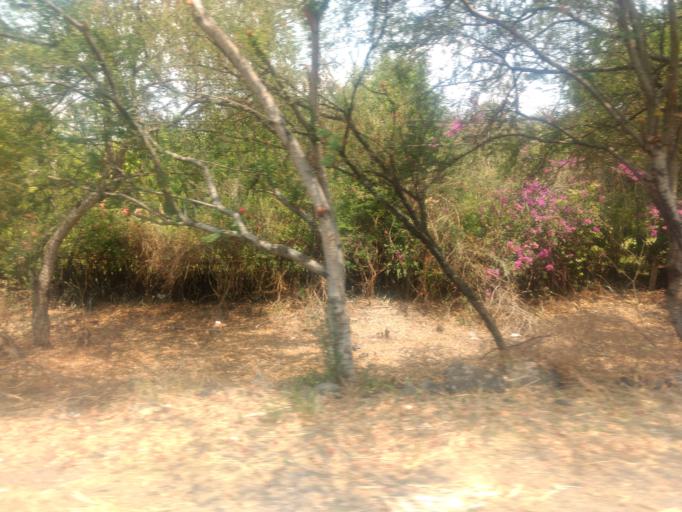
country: MX
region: Morelos
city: Puente de Ixtla
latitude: 18.6399
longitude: -99.3085
